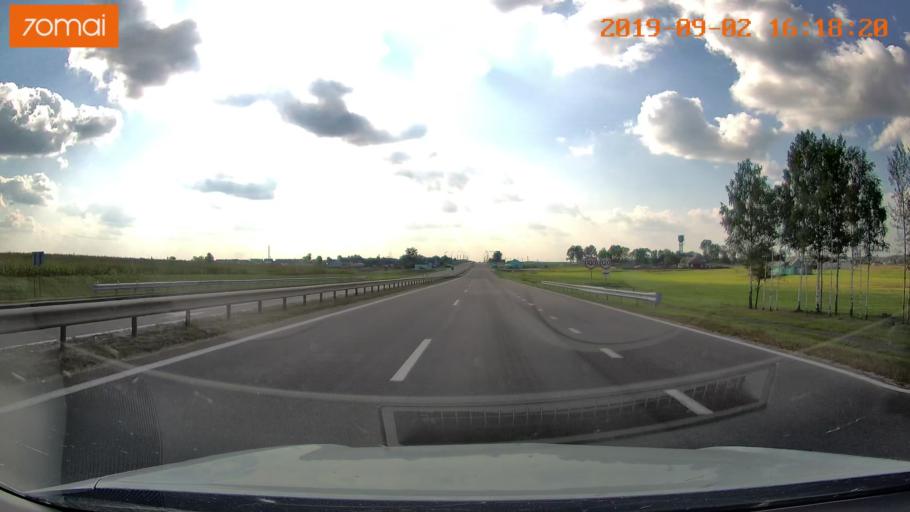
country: BY
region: Minsk
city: Chervyen'
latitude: 53.7300
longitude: 28.4419
